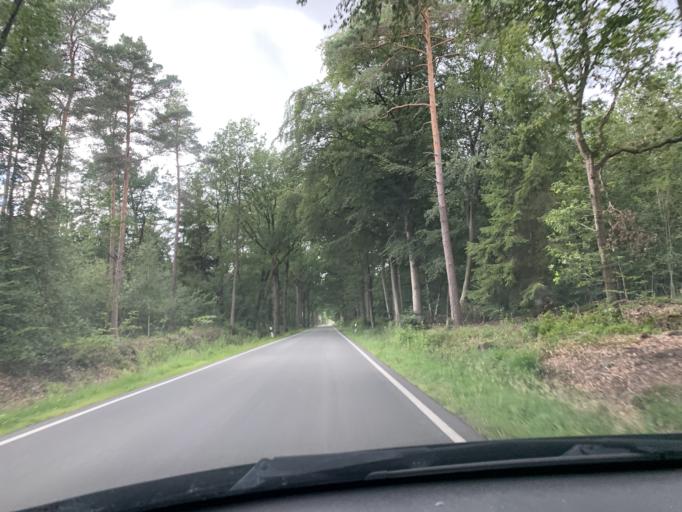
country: DE
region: Lower Saxony
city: Westerstede
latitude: 53.2192
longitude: 7.9118
